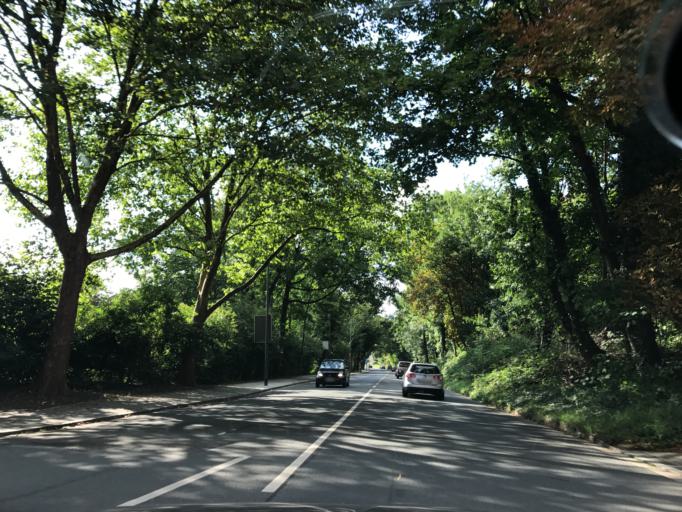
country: DE
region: North Rhine-Westphalia
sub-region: Regierungsbezirk Dusseldorf
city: Velbert
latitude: 51.3863
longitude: 7.0258
